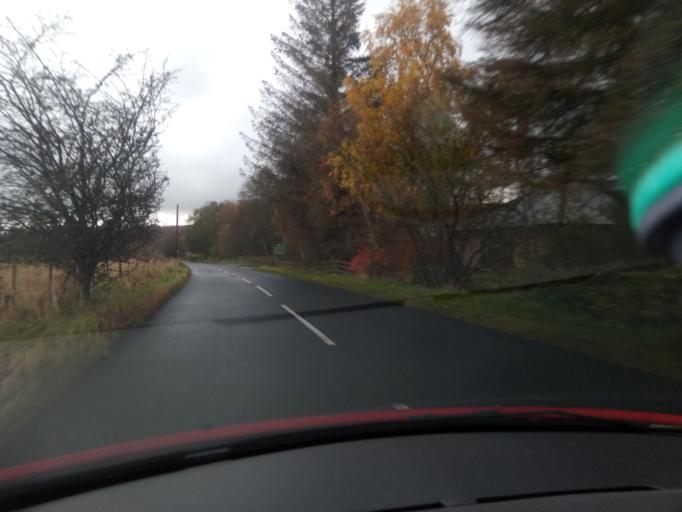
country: GB
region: England
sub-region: Northumberland
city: Birtley
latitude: 55.1370
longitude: -2.2587
